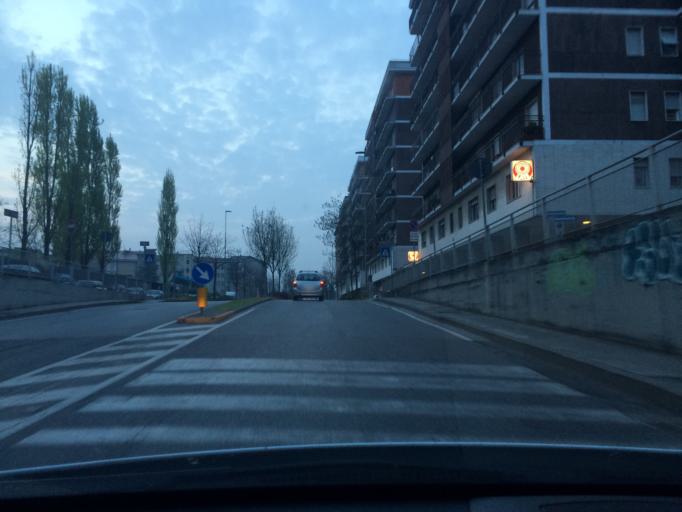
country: IT
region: Lombardy
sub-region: Provincia di Brescia
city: Brescia
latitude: 45.5189
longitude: 10.2213
